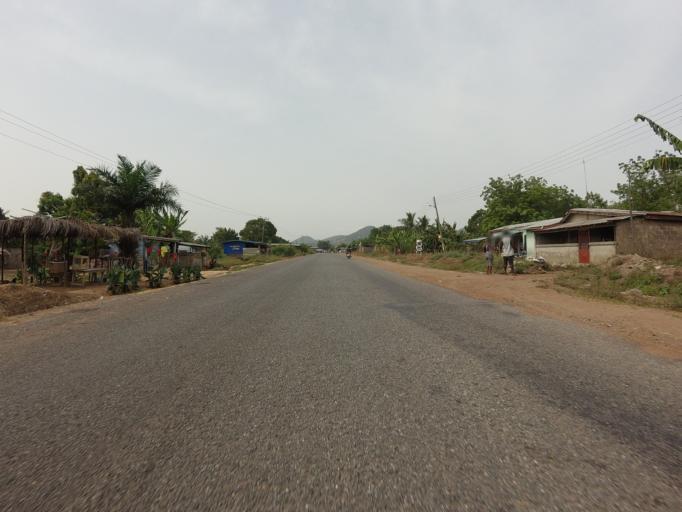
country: GH
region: Volta
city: Ho
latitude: 6.4179
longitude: 0.1765
